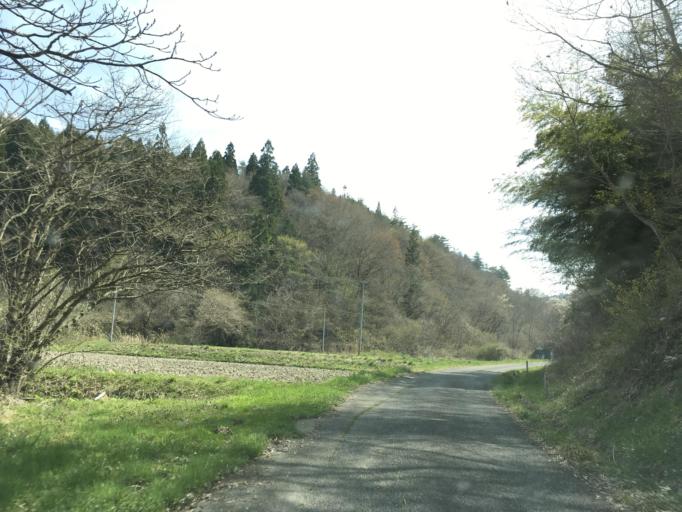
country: JP
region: Iwate
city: Ichinoseki
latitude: 38.8236
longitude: 141.3472
